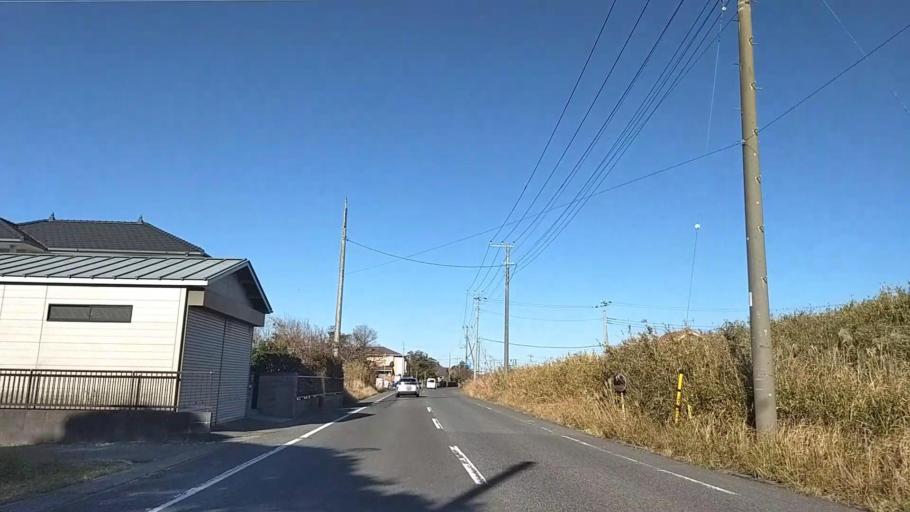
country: JP
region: Chiba
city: Mobara
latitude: 35.4119
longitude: 140.3887
